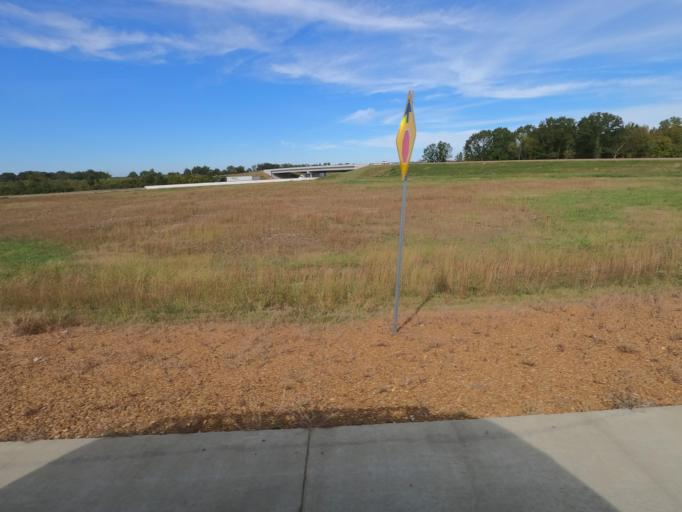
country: US
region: Tennessee
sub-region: Fayette County
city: Hickory Withe
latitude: 35.2898
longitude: -89.6097
